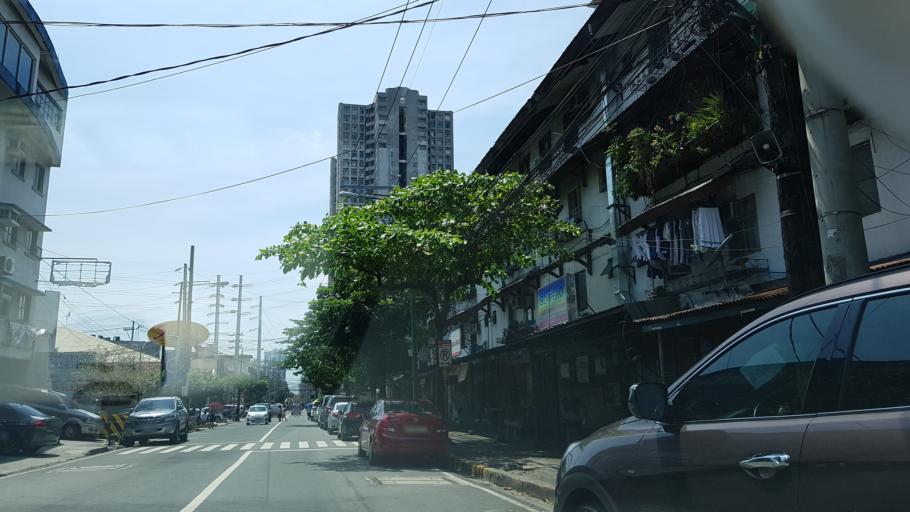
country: PH
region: Metro Manila
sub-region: Makati City
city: Makati City
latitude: 14.5666
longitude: 121.0145
